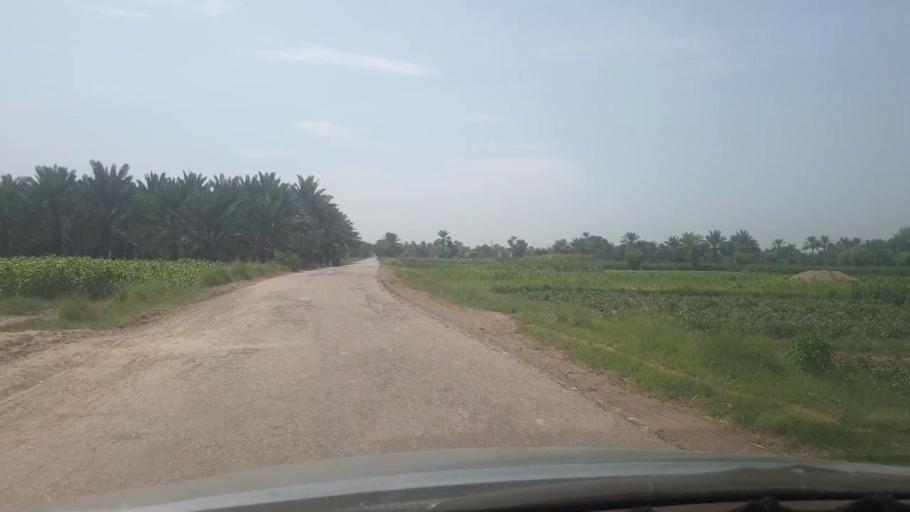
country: PK
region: Sindh
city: Bozdar
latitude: 27.2105
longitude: 68.5764
